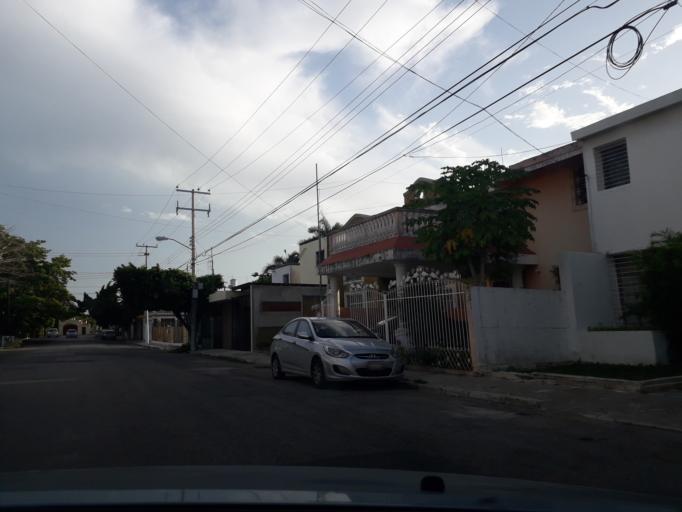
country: MX
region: Yucatan
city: Merida
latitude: 21.0078
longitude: -89.6390
